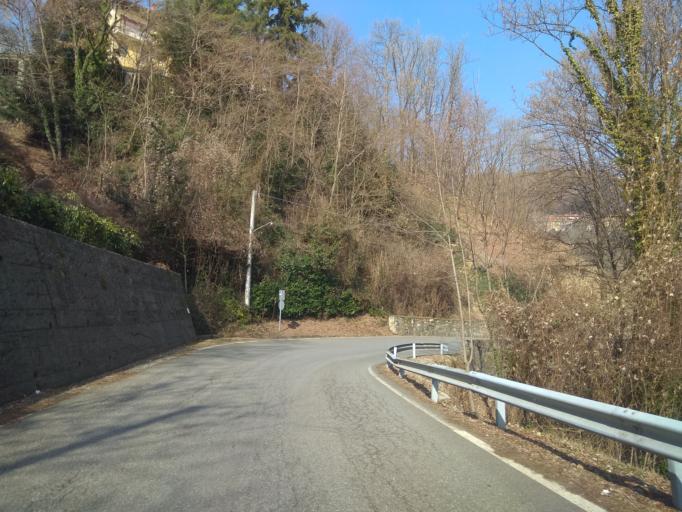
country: IT
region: Piedmont
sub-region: Provincia di Biella
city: Mosso
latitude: 45.6489
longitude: 8.1419
